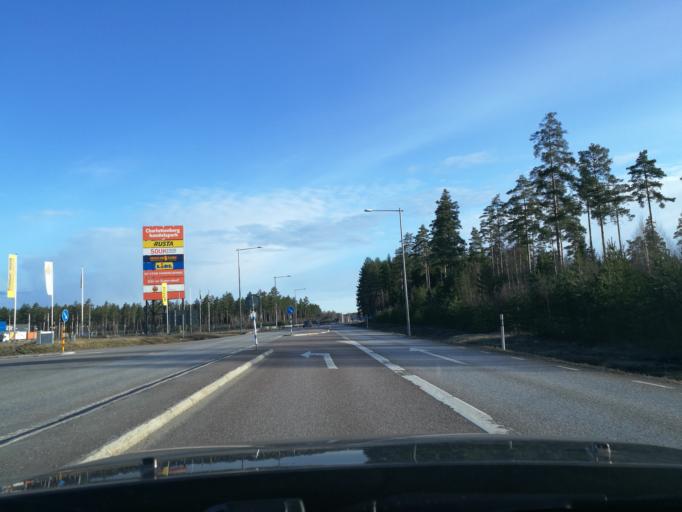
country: SE
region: Vaermland
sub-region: Eda Kommun
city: Charlottenberg
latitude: 59.8723
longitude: 12.2892
